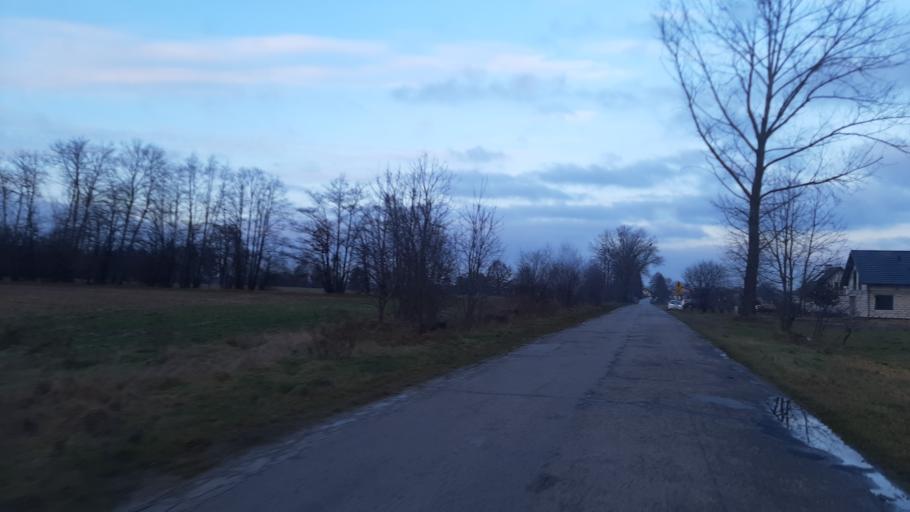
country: PL
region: Lublin Voivodeship
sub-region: Powiat lubartowski
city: Kamionka
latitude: 51.3975
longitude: 22.4105
